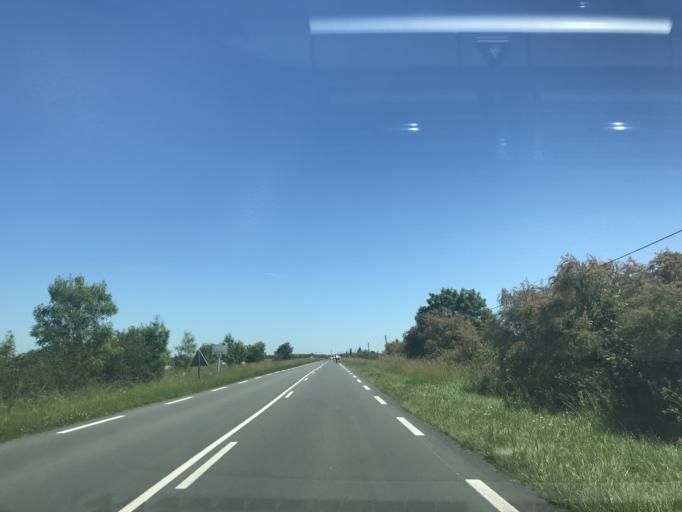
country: FR
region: Poitou-Charentes
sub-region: Departement de la Charente-Maritime
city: Meschers-sur-Gironde
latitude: 45.5617
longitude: -0.9358
